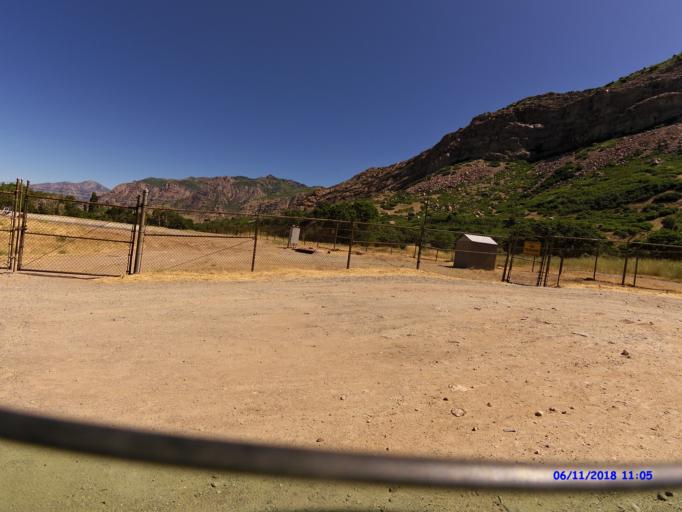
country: US
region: Utah
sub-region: Weber County
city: Ogden
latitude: 41.2191
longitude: -111.9306
